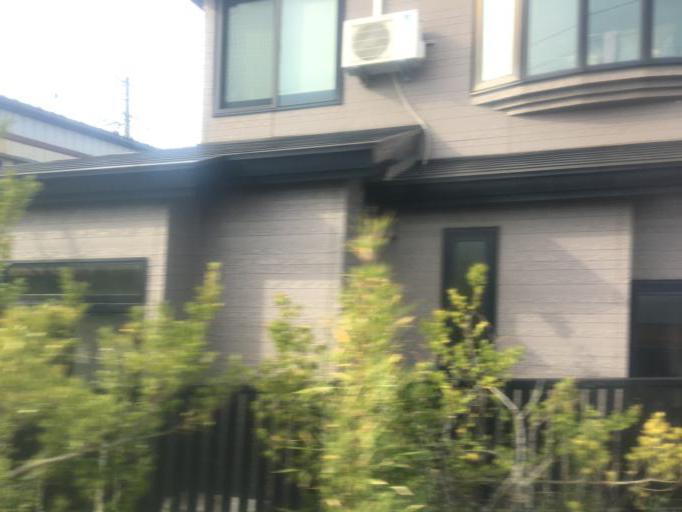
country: JP
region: Akita
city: Tenno
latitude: 39.8681
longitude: 140.0618
